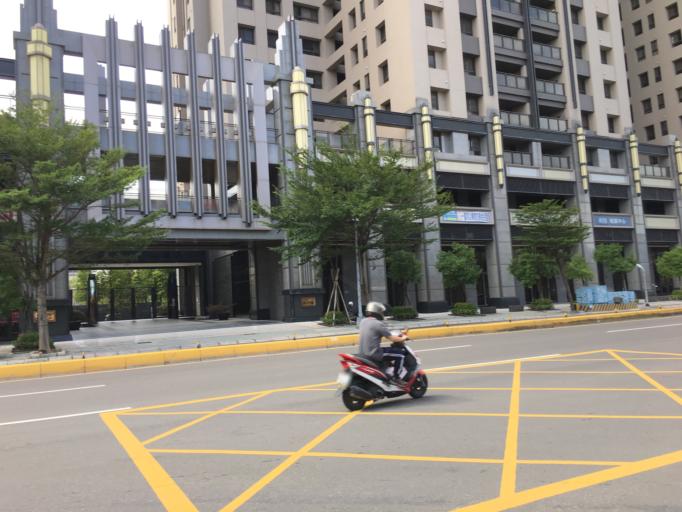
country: TW
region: Taiwan
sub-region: Hsinchu
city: Hsinchu
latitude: 24.7928
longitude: 121.0127
